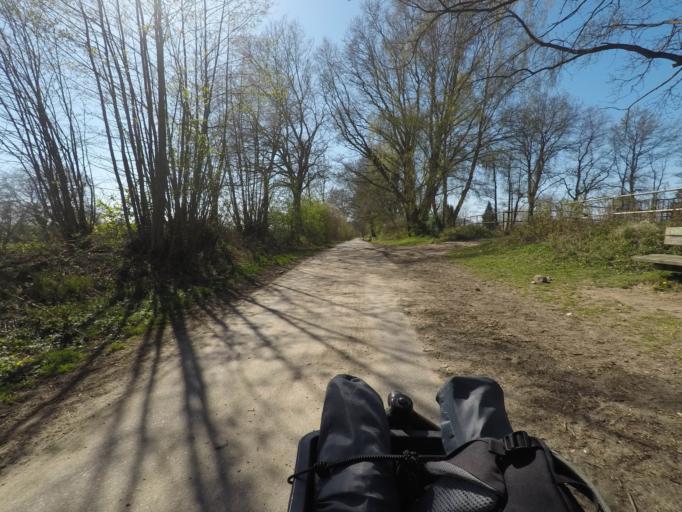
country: DE
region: Schleswig-Holstein
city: Stapelfeld
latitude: 53.6013
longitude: 10.2025
